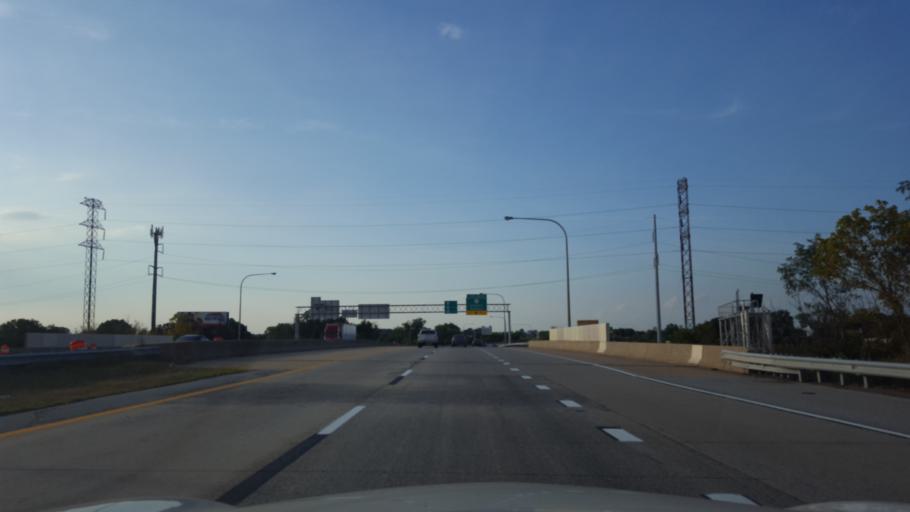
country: US
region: Delaware
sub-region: New Castle County
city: Newport
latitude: 39.7299
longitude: -75.6197
